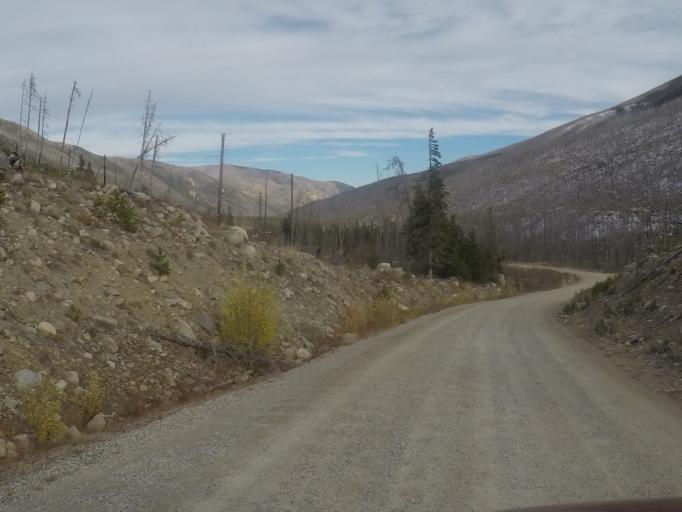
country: US
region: Montana
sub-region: Carbon County
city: Red Lodge
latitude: 45.1725
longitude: -109.4730
